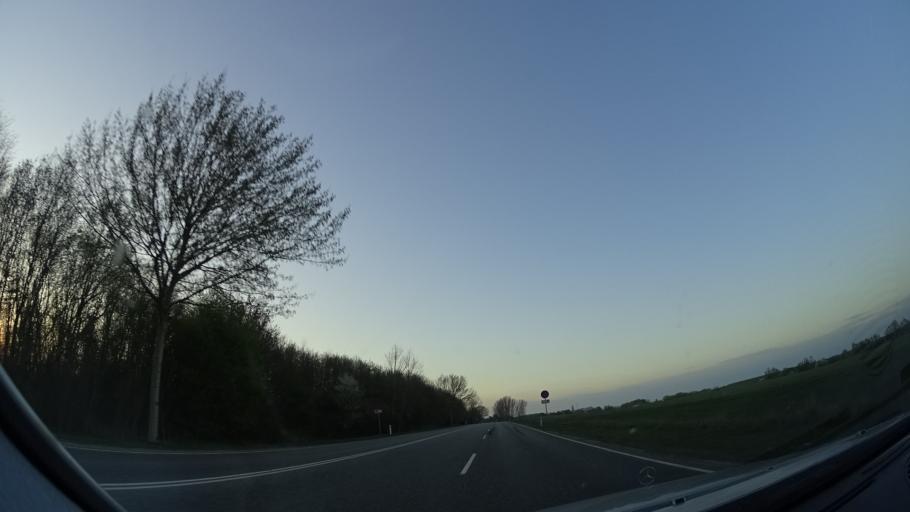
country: DK
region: Zealand
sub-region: Roskilde Kommune
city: Vindinge
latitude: 55.6041
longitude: 12.1006
